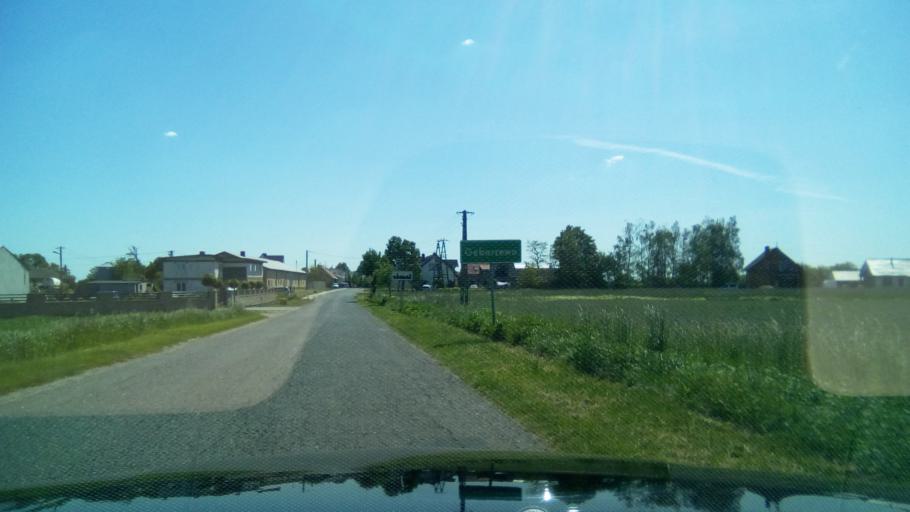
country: PL
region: Greater Poland Voivodeship
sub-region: Powiat gnieznienski
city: Gniezno
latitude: 52.4705
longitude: 17.5619
